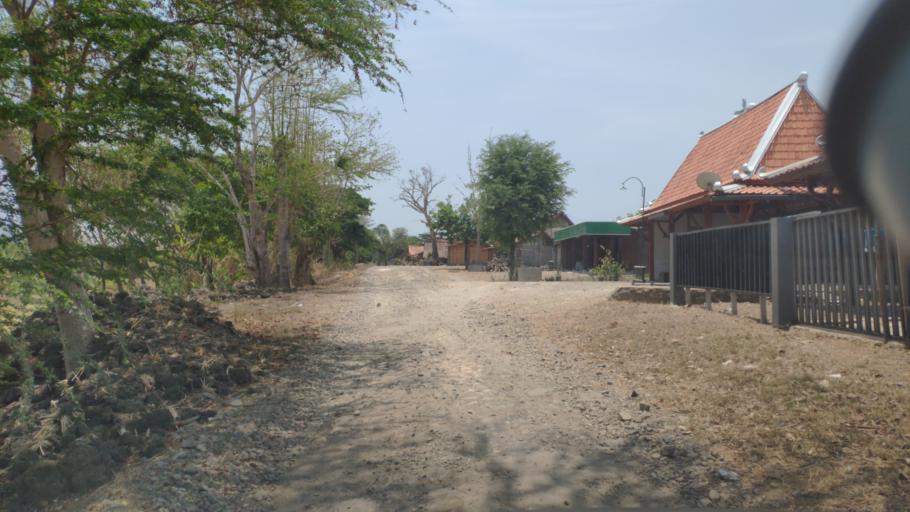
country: ID
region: Central Java
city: Randublatung
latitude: -7.1983
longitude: 111.2660
